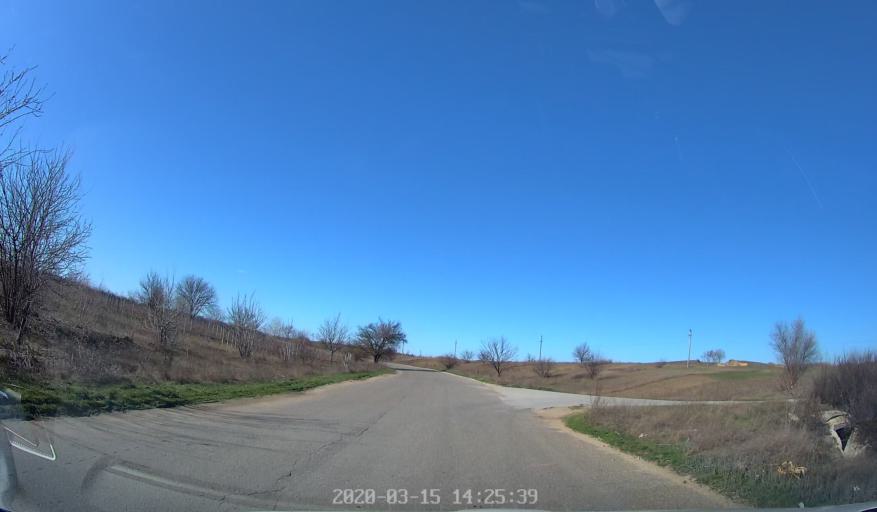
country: MD
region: Orhei
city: Orhei
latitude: 47.3400
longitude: 28.9161
